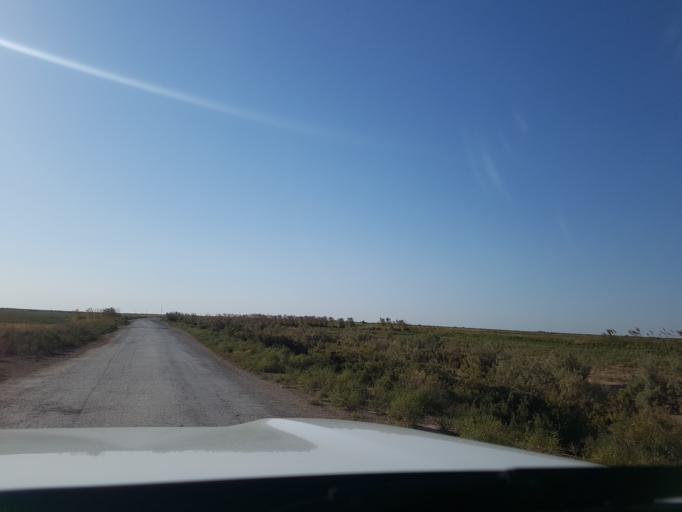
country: IR
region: Razavi Khorasan
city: Sarakhs
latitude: 36.9967
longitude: 61.3847
